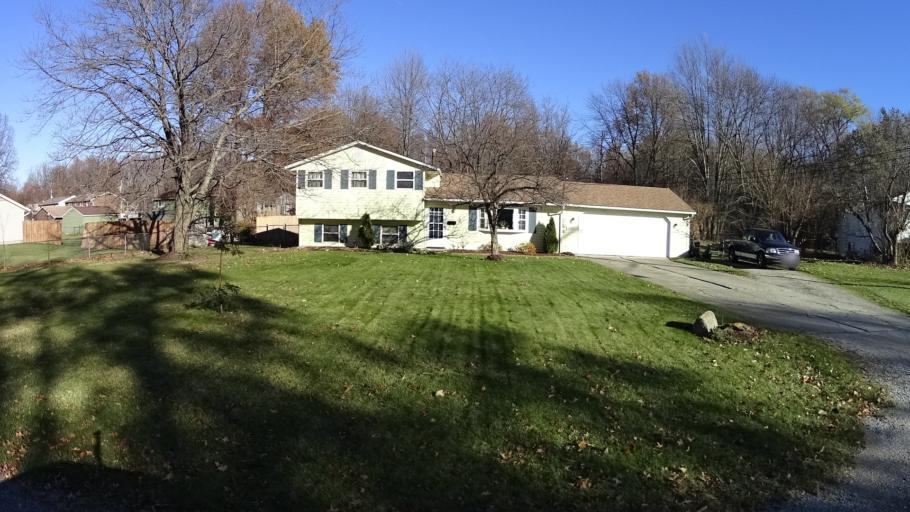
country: US
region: Ohio
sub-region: Lorain County
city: North Ridgeville
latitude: 41.3937
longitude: -82.0141
